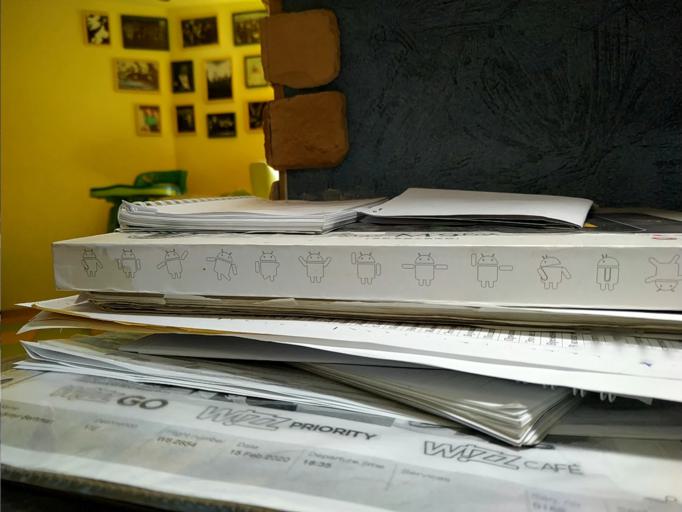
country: RU
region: Novgorod
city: Sol'tsy
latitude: 58.0431
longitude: 30.1900
